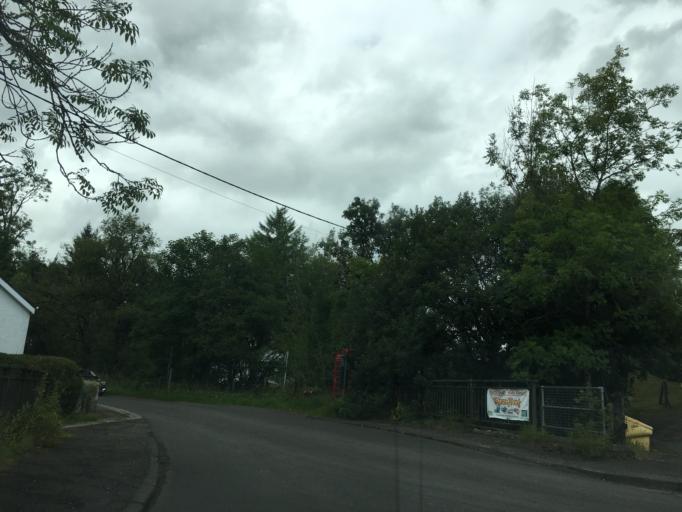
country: GB
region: Scotland
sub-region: Argyll and Bute
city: Oban
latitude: 56.3566
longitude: -5.1762
